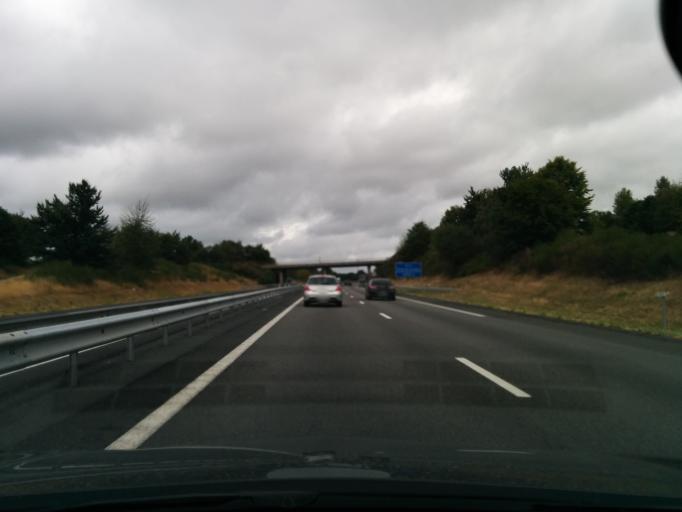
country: FR
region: Limousin
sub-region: Departement de la Haute-Vienne
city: Saint-Germain-les-Belles
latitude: 45.5257
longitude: 1.5144
